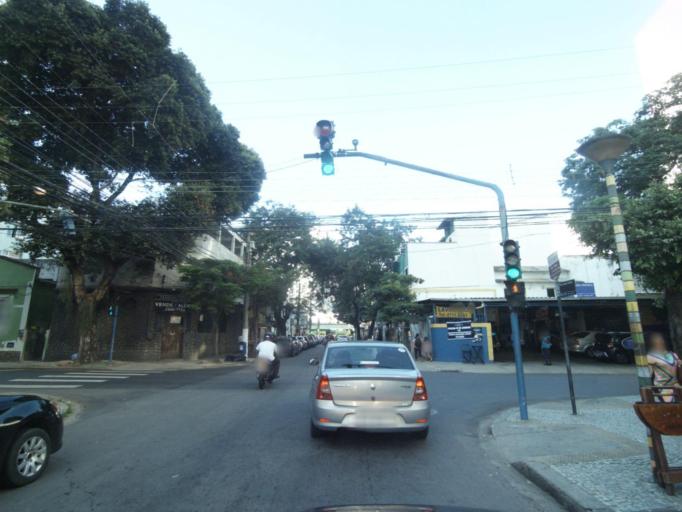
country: BR
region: Rio de Janeiro
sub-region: Niteroi
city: Niteroi
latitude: -22.8996
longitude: -43.1040
